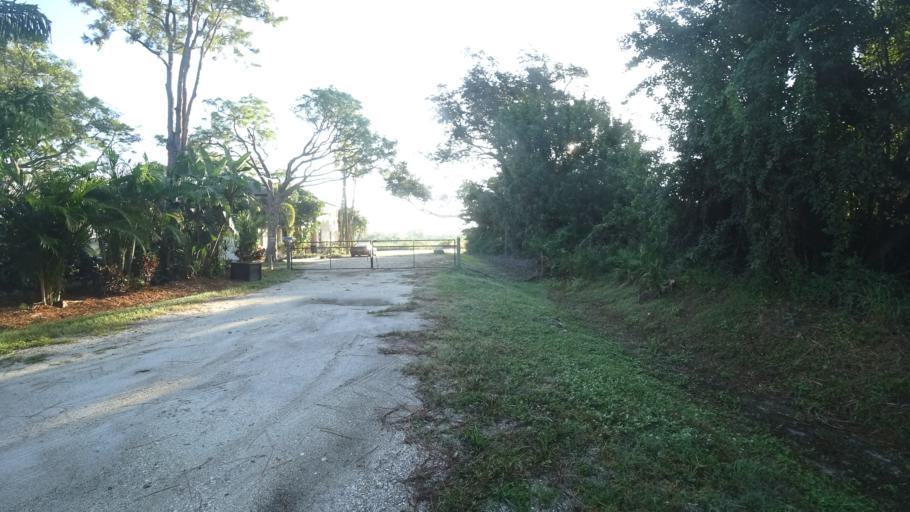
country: US
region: Florida
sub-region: Manatee County
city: Samoset
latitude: 27.4600
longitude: -82.4962
